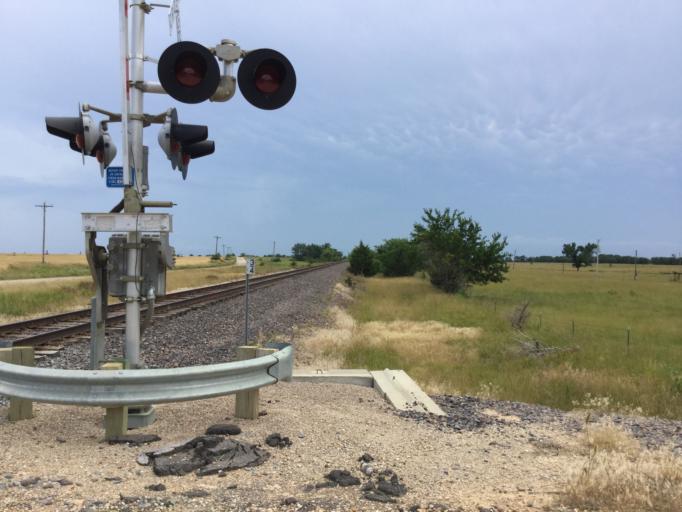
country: US
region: Kansas
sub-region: Woodson County
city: Yates Center
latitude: 38.0098
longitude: -95.6468
